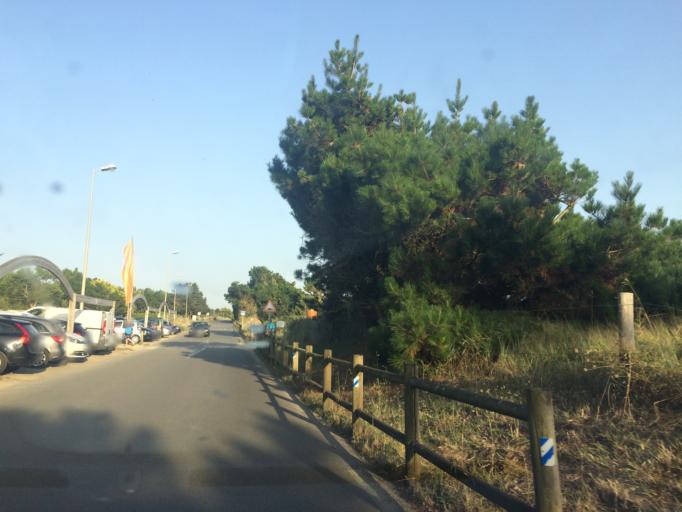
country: FR
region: Brittany
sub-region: Departement du Morbihan
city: Damgan
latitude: 47.5156
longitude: -2.5645
